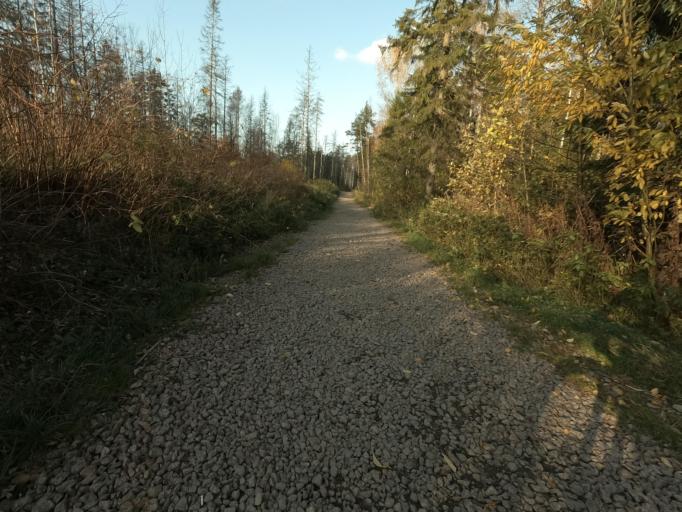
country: RU
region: Leningrad
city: Sertolovo
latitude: 60.1481
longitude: 30.2222
